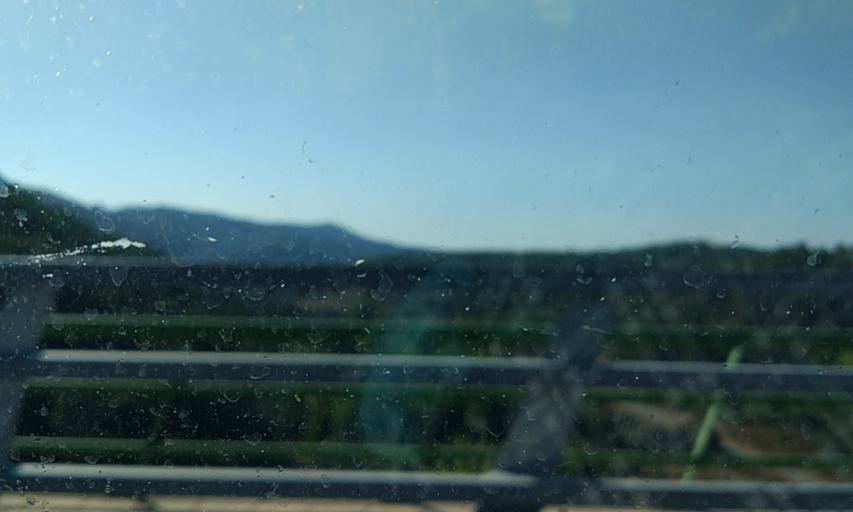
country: PT
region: Vila Real
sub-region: Murca
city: Murca
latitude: 41.4124
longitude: -7.4170
